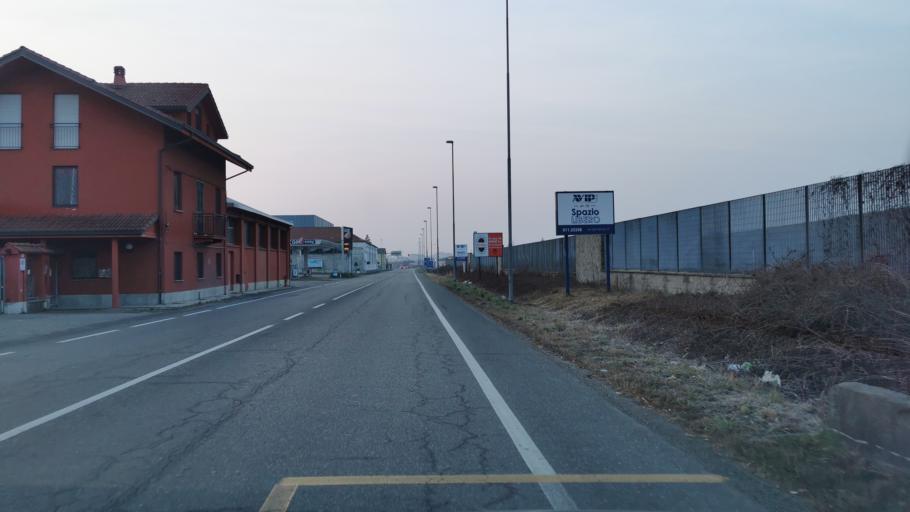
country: IT
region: Piedmont
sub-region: Provincia di Torino
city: Borgaro Torinese
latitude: 45.1379
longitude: 7.6560
